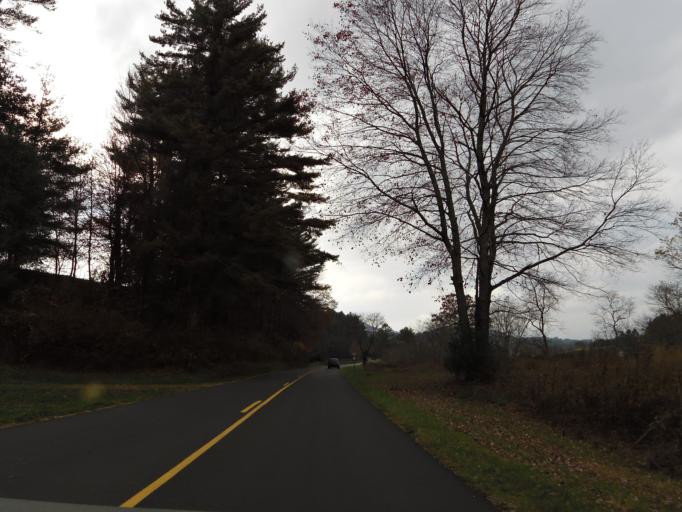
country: US
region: North Carolina
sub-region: Wilkes County
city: Mulberry
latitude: 36.3912
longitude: -81.2389
